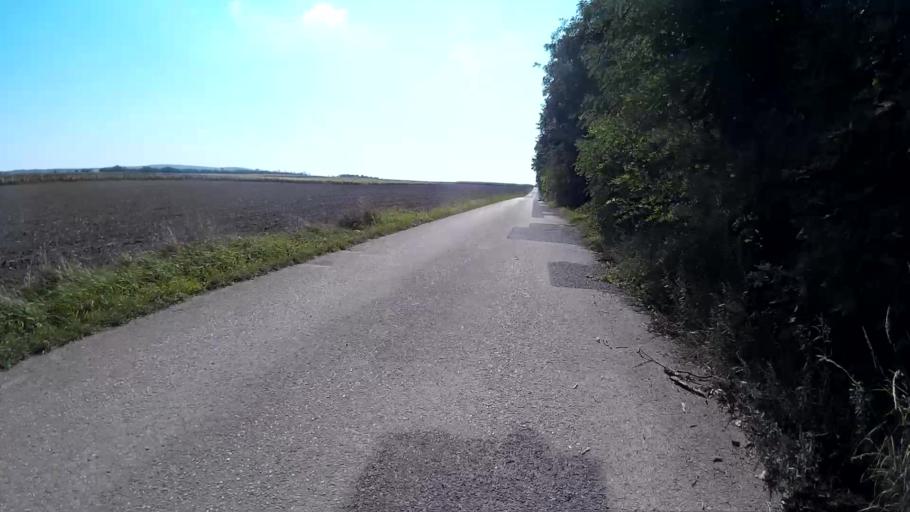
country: AT
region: Lower Austria
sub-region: Politischer Bezirk Mistelbach
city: Neudorf bei Staatz
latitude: 48.7717
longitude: 16.4882
